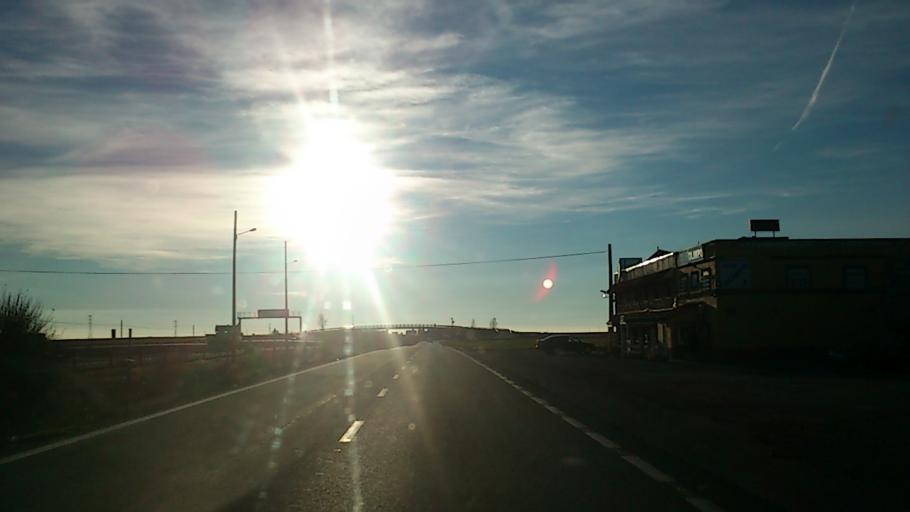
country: ES
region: Castille-La Mancha
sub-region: Provincia de Guadalajara
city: Almadrones
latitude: 40.8926
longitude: -2.7688
